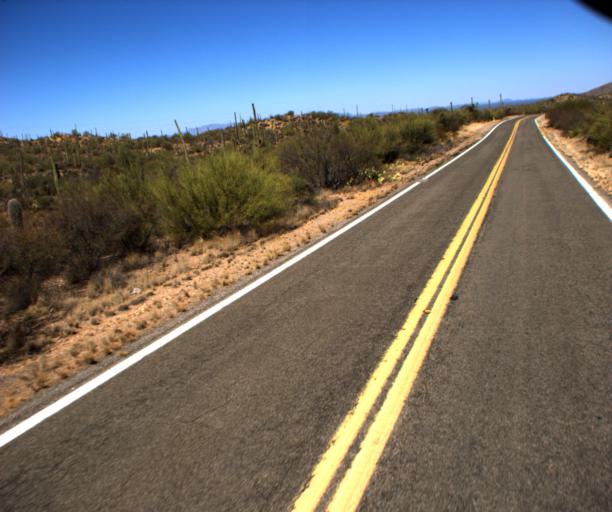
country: US
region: Arizona
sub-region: Pima County
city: Sells
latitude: 32.1755
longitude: -112.1862
